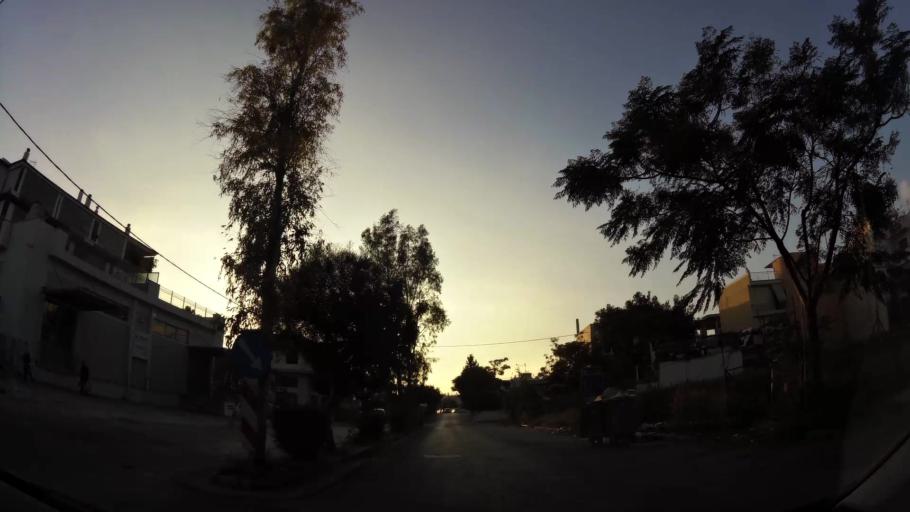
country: GR
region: Attica
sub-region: Nomarchia Anatolikis Attikis
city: Acharnes
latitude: 38.0931
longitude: 23.7406
